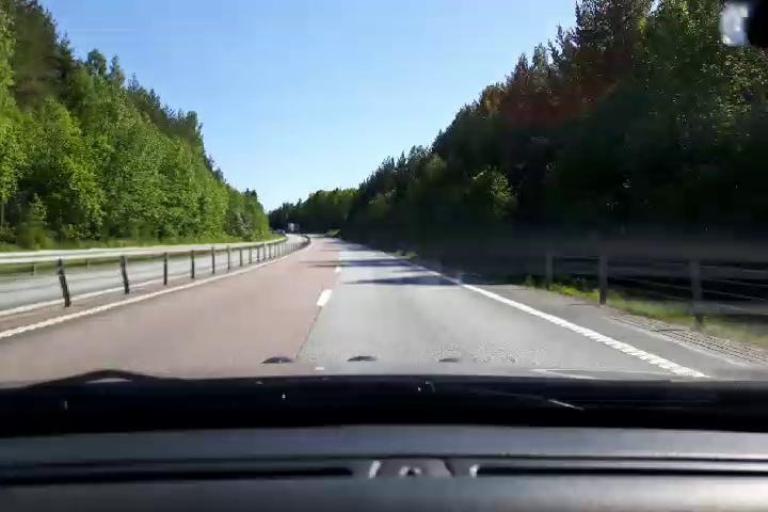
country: SE
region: Gaevleborg
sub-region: Soderhamns Kommun
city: Soderhamn
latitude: 61.2728
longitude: 17.0263
